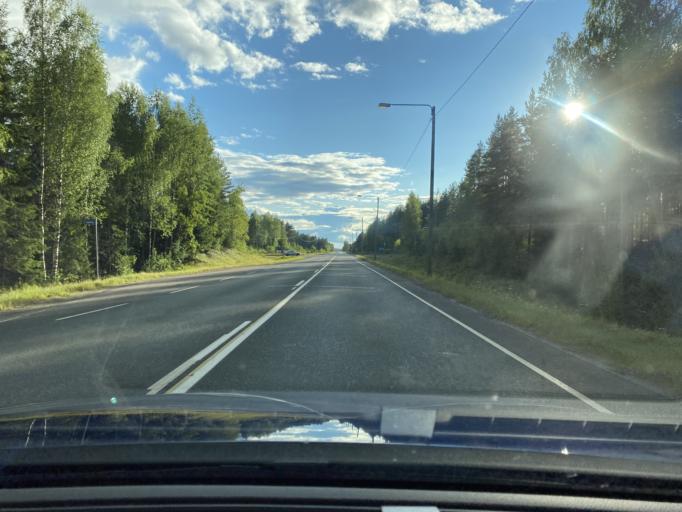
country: FI
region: Uusimaa
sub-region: Helsinki
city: Kaerkoelae
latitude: 60.8285
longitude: 24.0197
